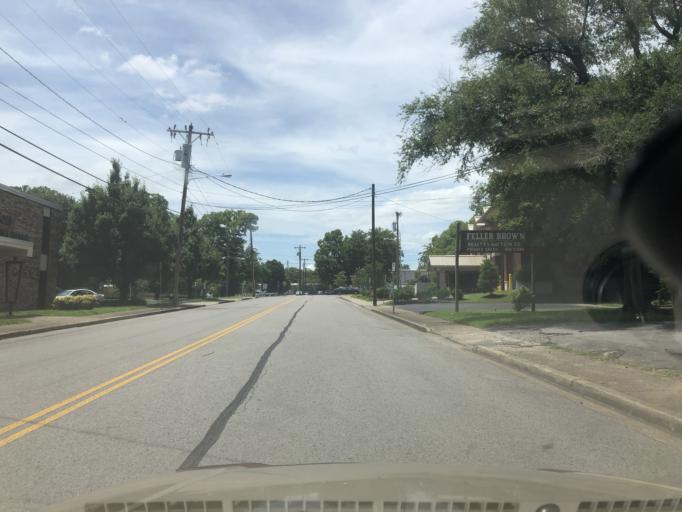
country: US
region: Tennessee
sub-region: Davidson County
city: Goodlettsville
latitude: 36.2587
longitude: -86.7151
